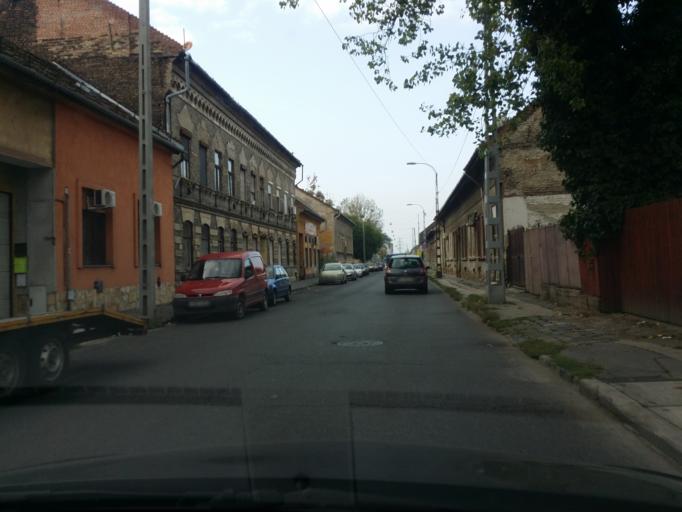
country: HU
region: Budapest
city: Budapest IV. keruelet
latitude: 47.5682
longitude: 19.0837
